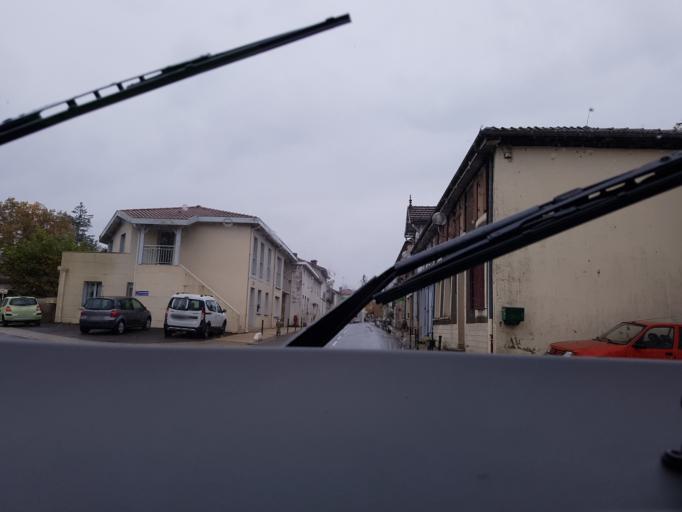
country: FR
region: Aquitaine
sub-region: Departement de la Gironde
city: Saint-Symphorien
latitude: 44.3232
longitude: -0.5837
